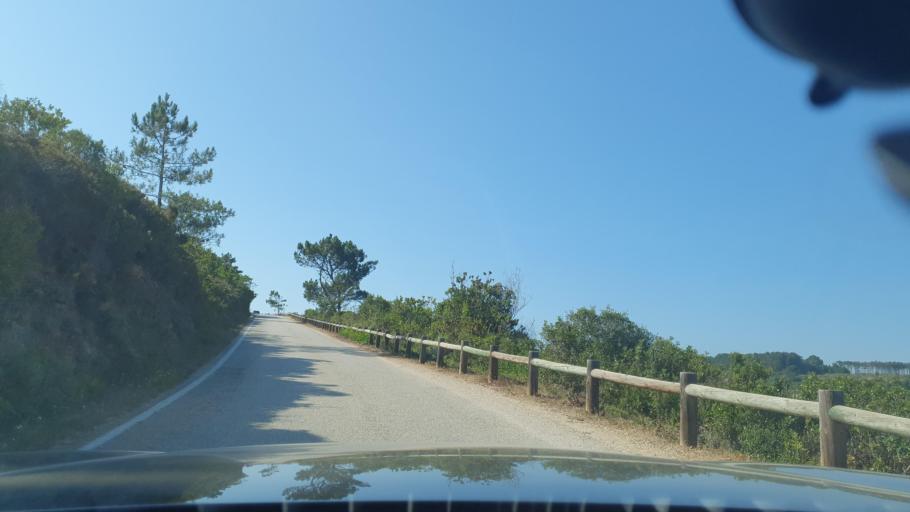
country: PT
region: Beja
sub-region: Odemira
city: Sao Teotonio
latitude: 37.4372
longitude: -8.7949
